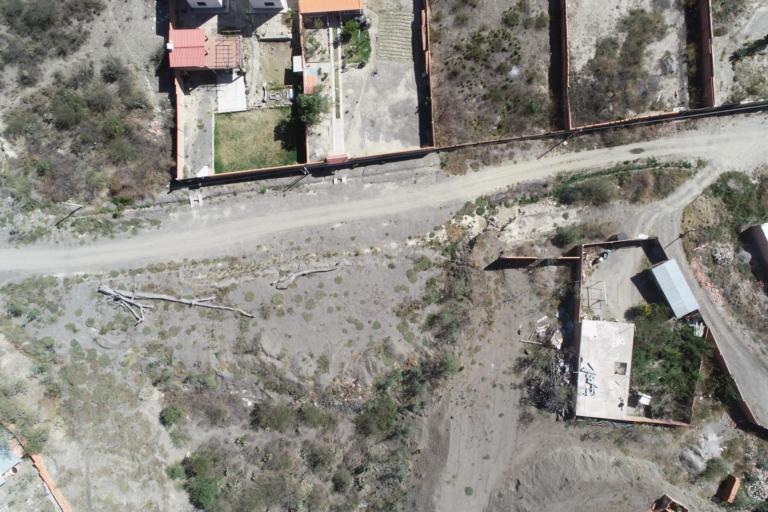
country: BO
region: La Paz
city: La Paz
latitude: -16.6333
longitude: -68.0462
